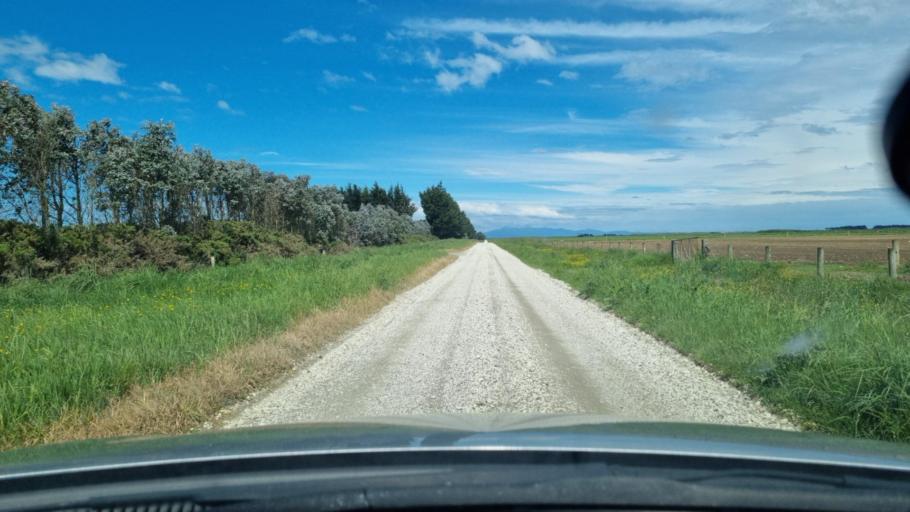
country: NZ
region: Southland
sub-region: Invercargill City
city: Invercargill
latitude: -46.3720
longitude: 168.2774
